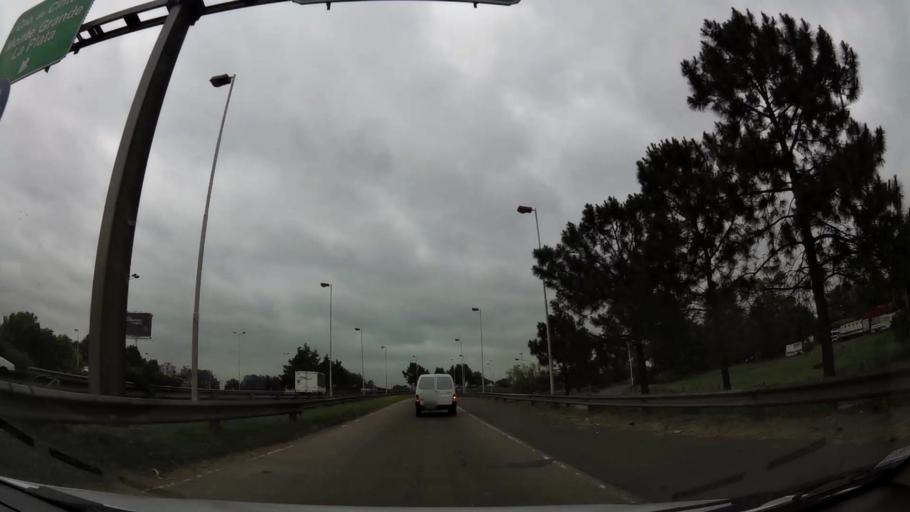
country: AR
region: Buenos Aires F.D.
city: Villa Lugano
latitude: -34.7199
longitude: -58.5123
